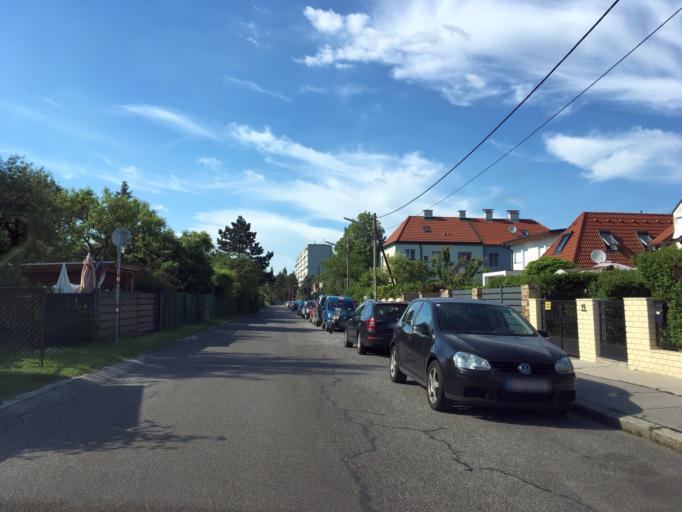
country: AT
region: Lower Austria
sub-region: Politischer Bezirk Korneuburg
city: Langenzersdorf
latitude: 48.2730
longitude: 16.3857
